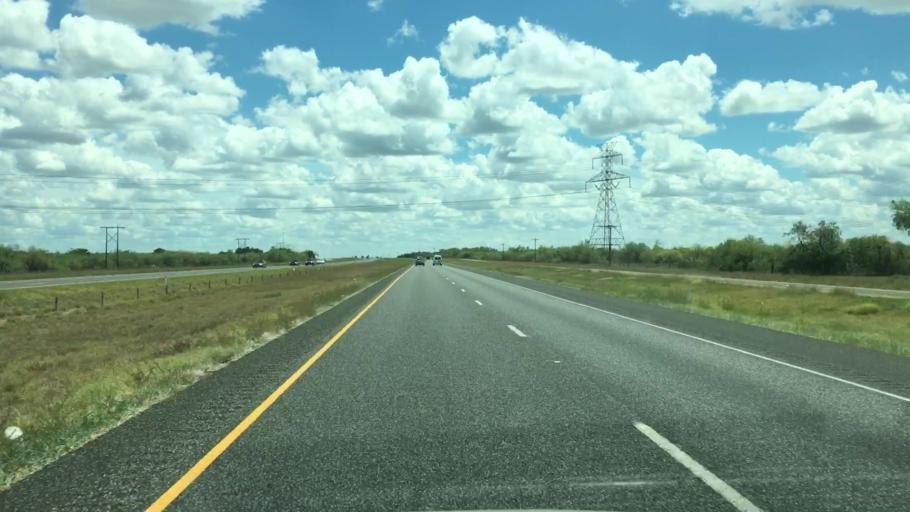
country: US
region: Texas
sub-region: Atascosa County
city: Pleasanton
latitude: 28.8235
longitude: -98.3638
